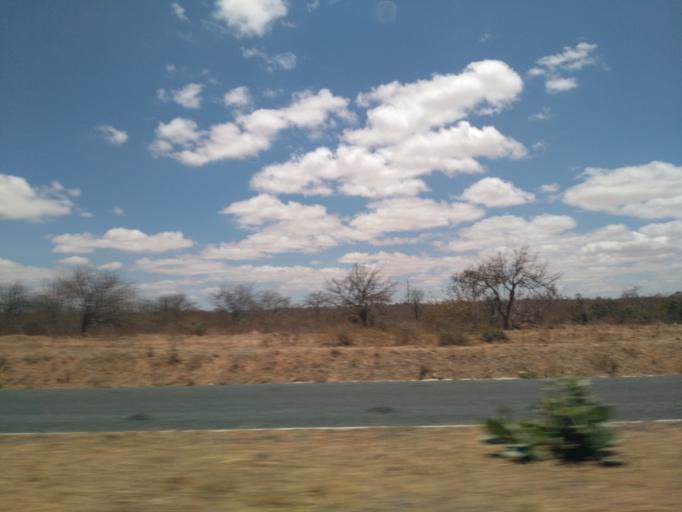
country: TZ
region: Dodoma
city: Kisasa
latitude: -6.1686
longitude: 35.8470
